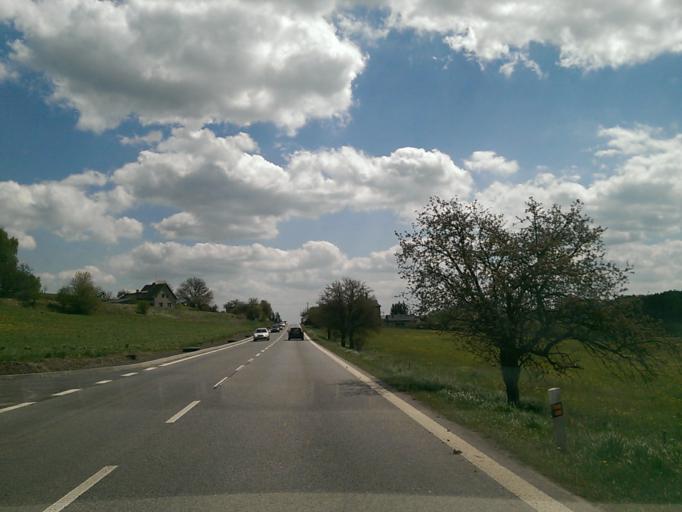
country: CZ
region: Liberecky
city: Rovensko pod Troskami
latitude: 50.5560
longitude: 15.2081
